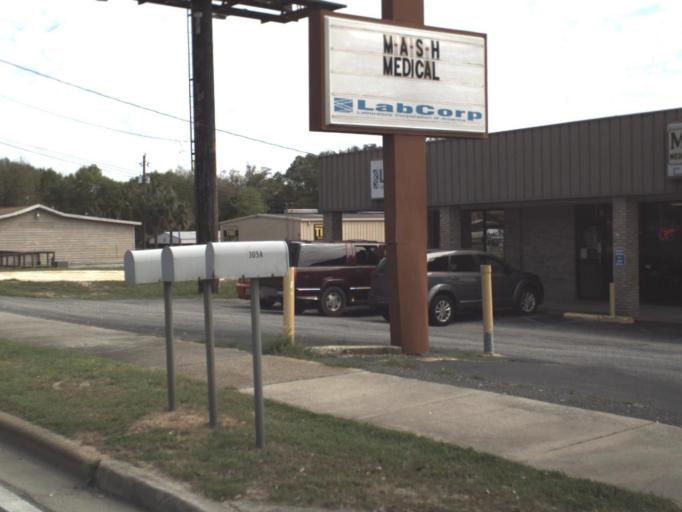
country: US
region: Florida
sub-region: Okaloosa County
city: Crestview
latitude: 30.7433
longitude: -86.5638
